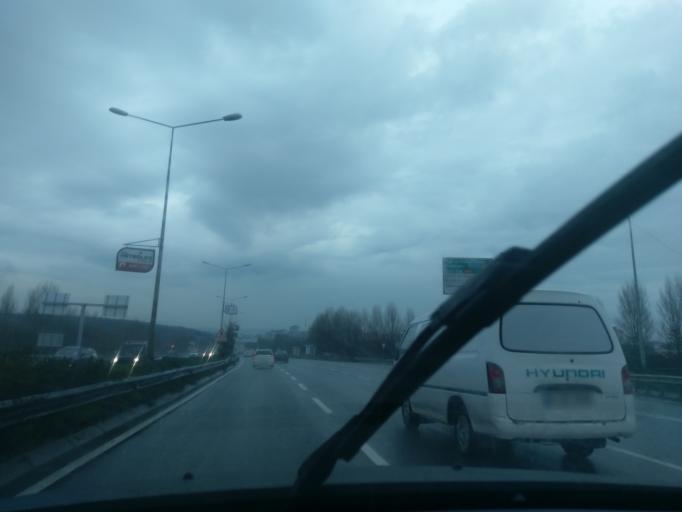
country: TR
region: Istanbul
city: Samandira
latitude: 41.0161
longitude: 29.2054
